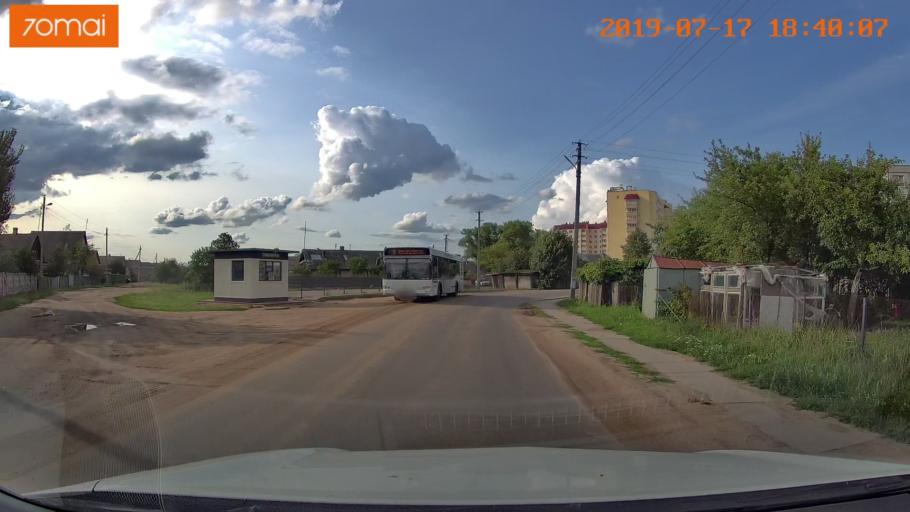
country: BY
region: Mogilev
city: Asipovichy
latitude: 53.3009
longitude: 28.6540
